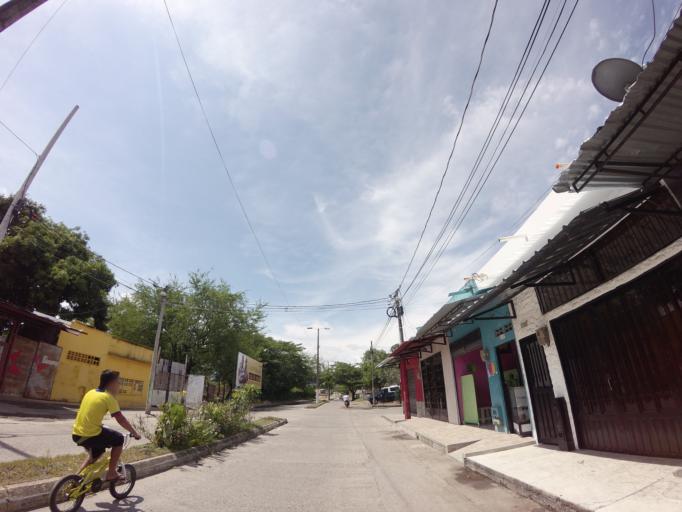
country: CO
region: Cundinamarca
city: Puerto Salgar
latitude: 5.4754
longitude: -74.6724
